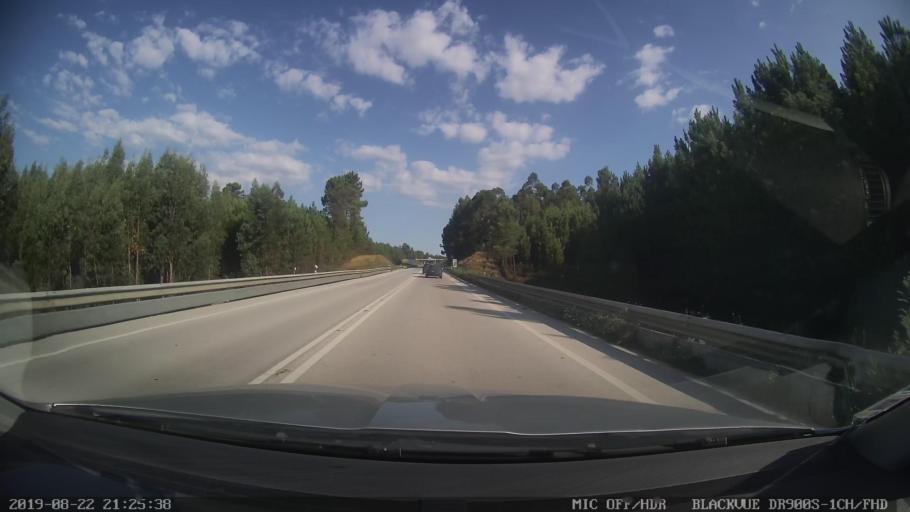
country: PT
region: Castelo Branco
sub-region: Serta
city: Serta
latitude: 39.8569
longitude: -8.1256
